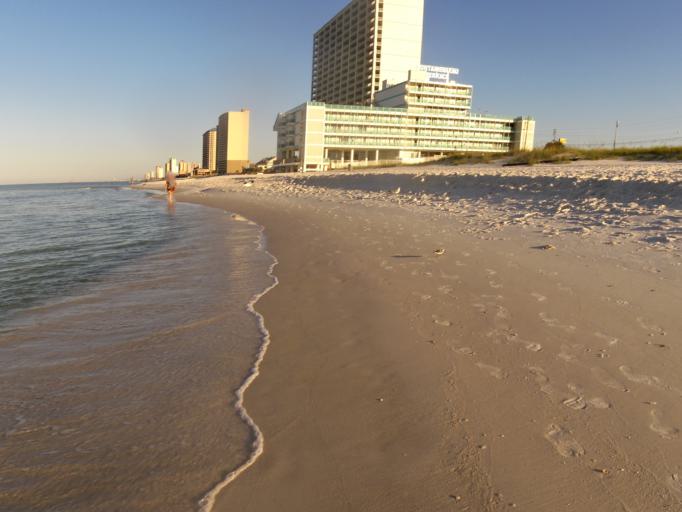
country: US
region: Florida
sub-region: Bay County
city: Panama City Beach
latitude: 30.2022
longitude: -85.8540
